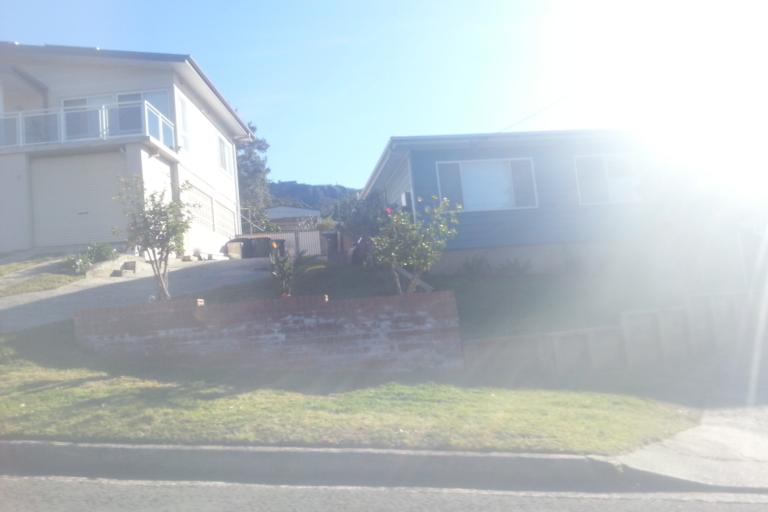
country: AU
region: New South Wales
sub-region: Wollongong
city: Bulli
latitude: -34.3156
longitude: 150.9091
